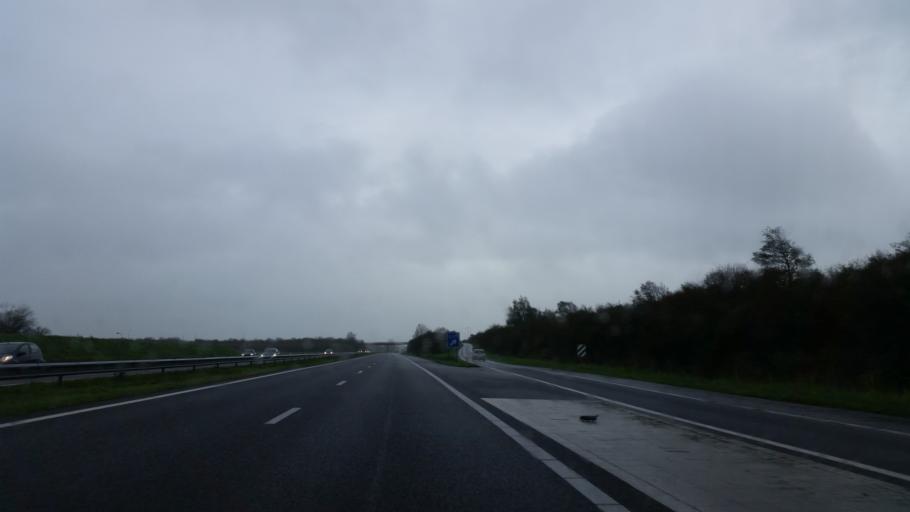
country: NL
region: Friesland
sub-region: Gemeente Boarnsterhim
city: Reduzum
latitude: 53.1164
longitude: 5.8103
